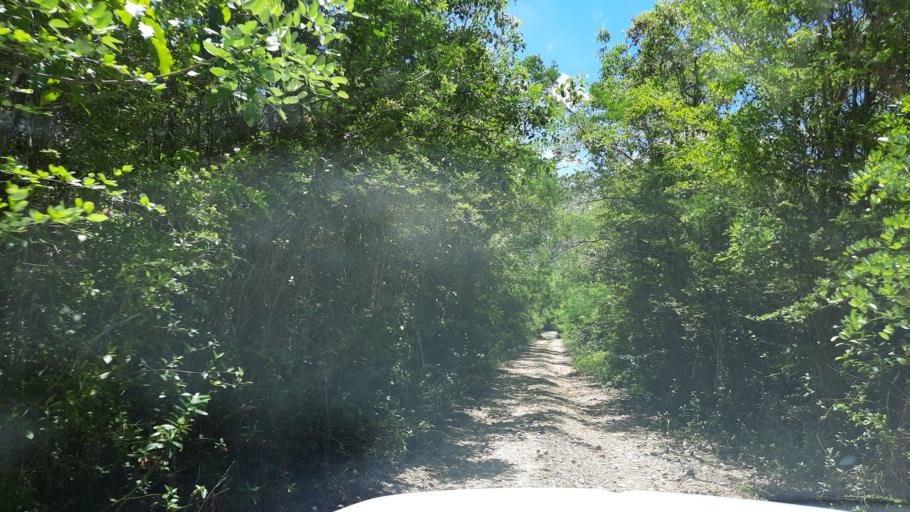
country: BZ
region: Cayo
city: Belmopan
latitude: 17.3559
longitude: -88.5435
